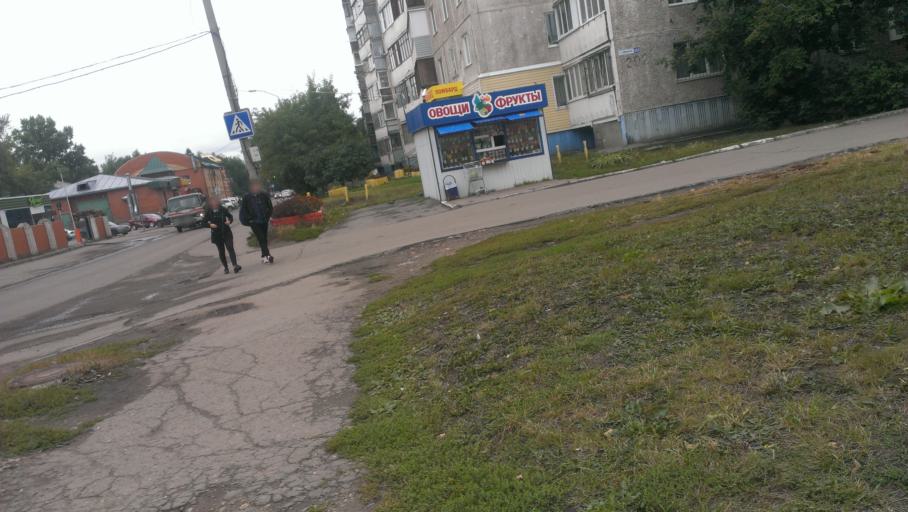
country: RU
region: Altai Krai
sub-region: Gorod Barnaulskiy
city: Barnaul
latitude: 53.3718
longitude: 83.6904
